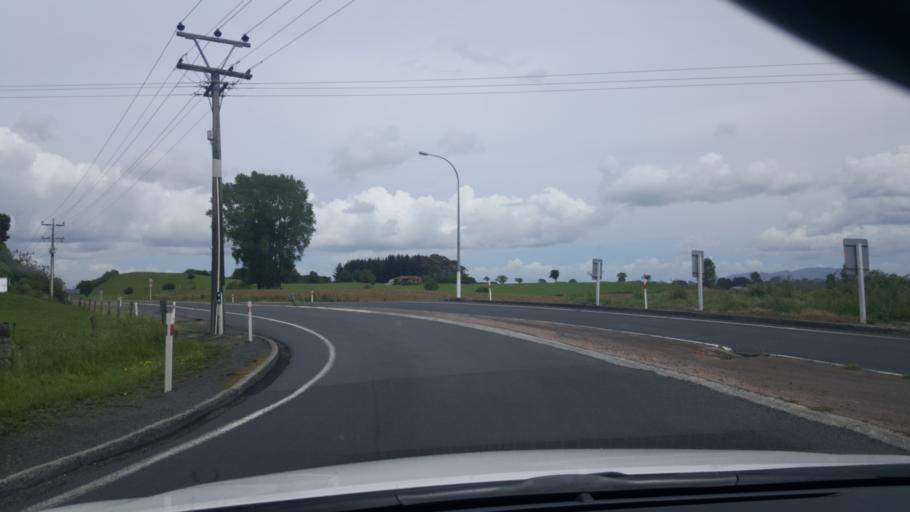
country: NZ
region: Waikato
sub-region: Matamata-Piako District
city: Matamata
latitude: -37.8887
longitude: 175.7758
